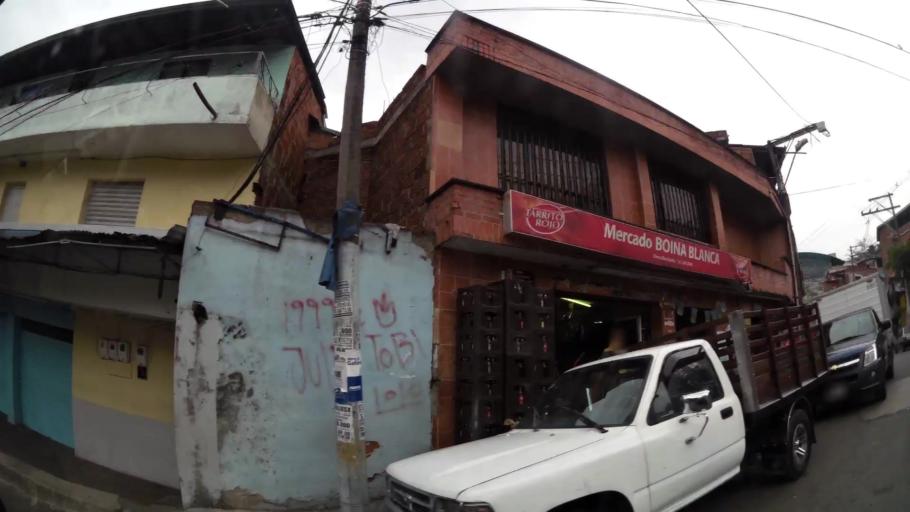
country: CO
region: Antioquia
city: Bello
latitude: 6.2949
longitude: -75.5529
